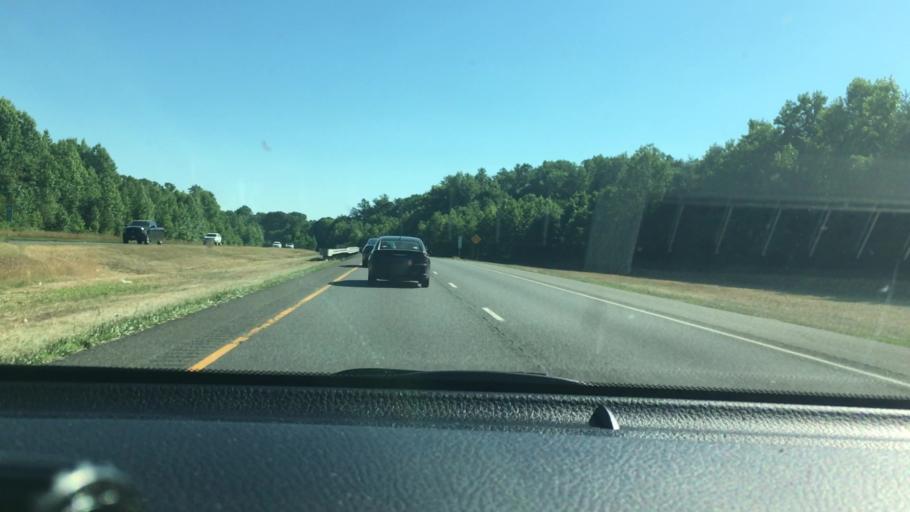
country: US
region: New Jersey
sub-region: Gloucester County
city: Pitman
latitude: 39.7445
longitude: -75.1456
